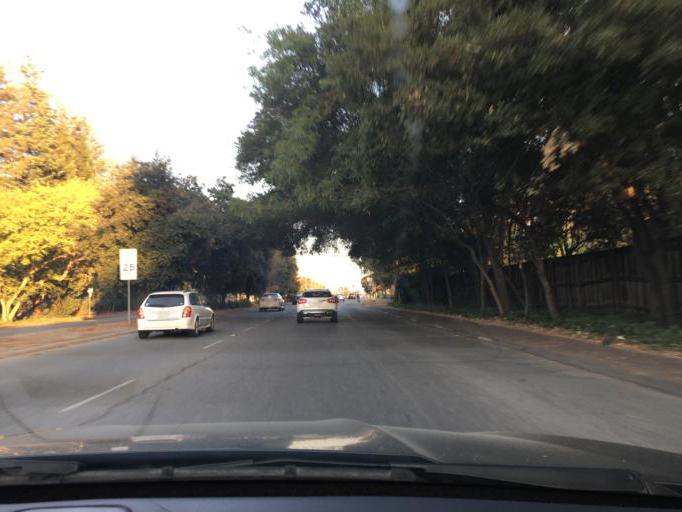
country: US
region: California
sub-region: Santa Clara County
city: Saratoga
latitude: 37.2931
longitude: -122.0047
